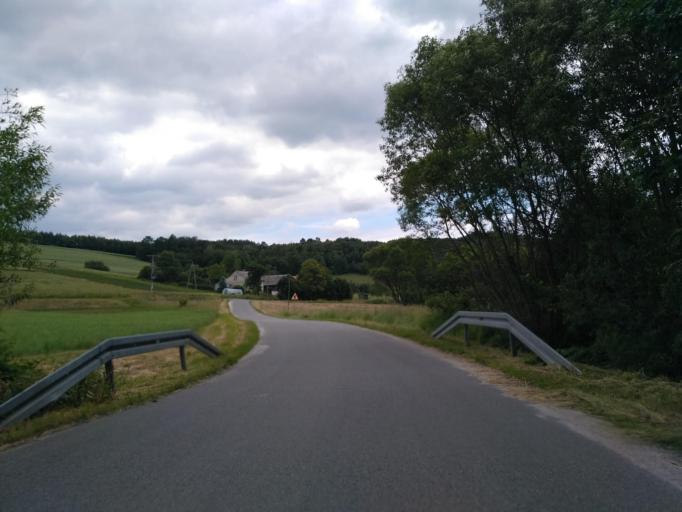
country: PL
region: Subcarpathian Voivodeship
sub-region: Powiat przeworski
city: Jawornik Polski
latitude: 49.8509
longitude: 22.2981
